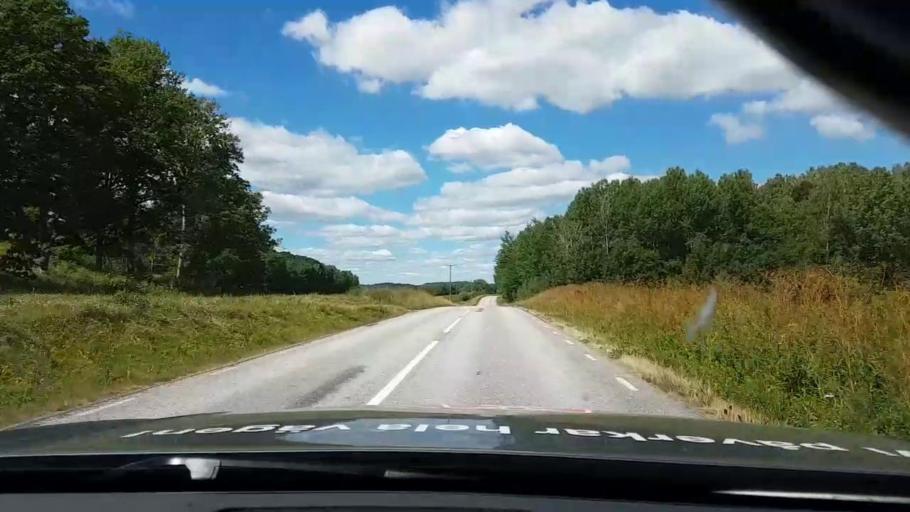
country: SE
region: Kalmar
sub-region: Vasterviks Kommun
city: Forserum
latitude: 58.0477
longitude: 16.4115
